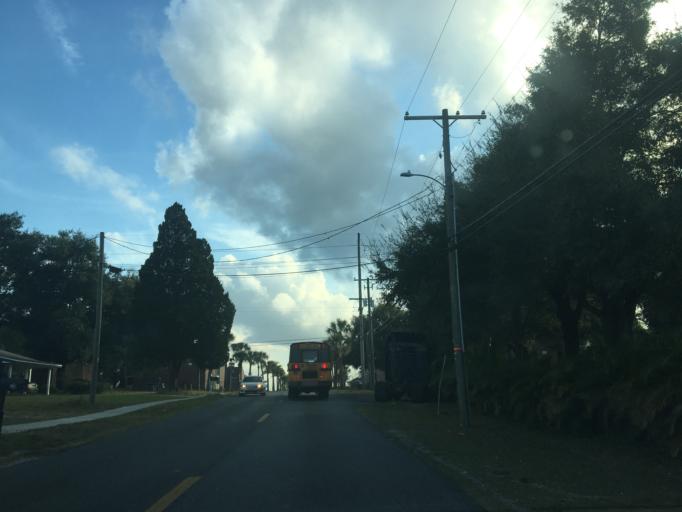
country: US
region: Florida
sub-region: Hillsborough County
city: Temple Terrace
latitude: 28.0295
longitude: -82.4017
